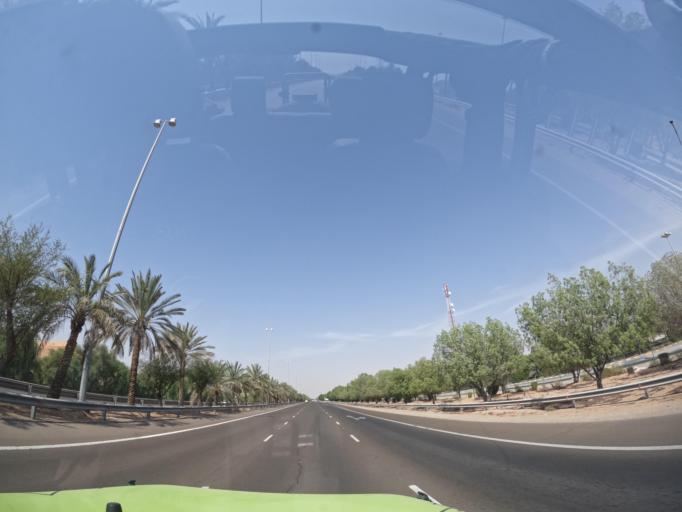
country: AE
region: Abu Dhabi
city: Al Ain
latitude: 24.2109
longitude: 55.5051
